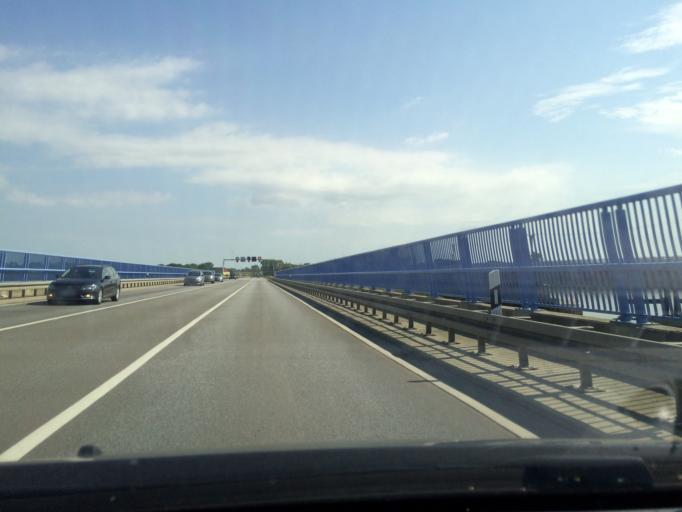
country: DE
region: Mecklenburg-Vorpommern
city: Altefahr
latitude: 54.3179
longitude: 13.1306
